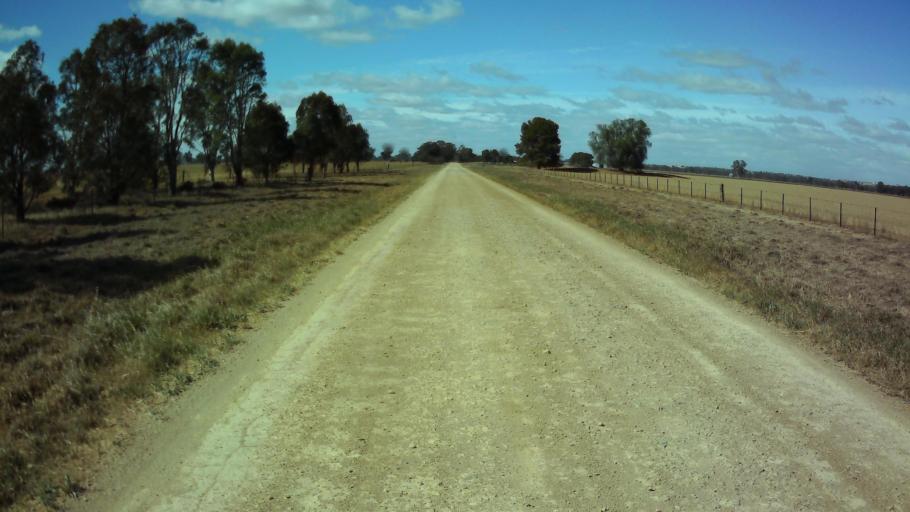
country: AU
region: New South Wales
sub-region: Weddin
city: Grenfell
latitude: -34.0209
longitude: 148.3190
